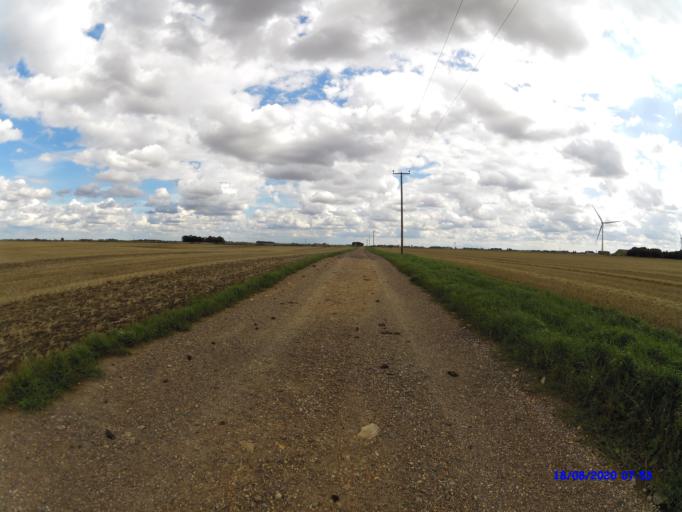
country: GB
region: England
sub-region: Cambridgeshire
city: Whittlesey
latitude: 52.5176
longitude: -0.0903
